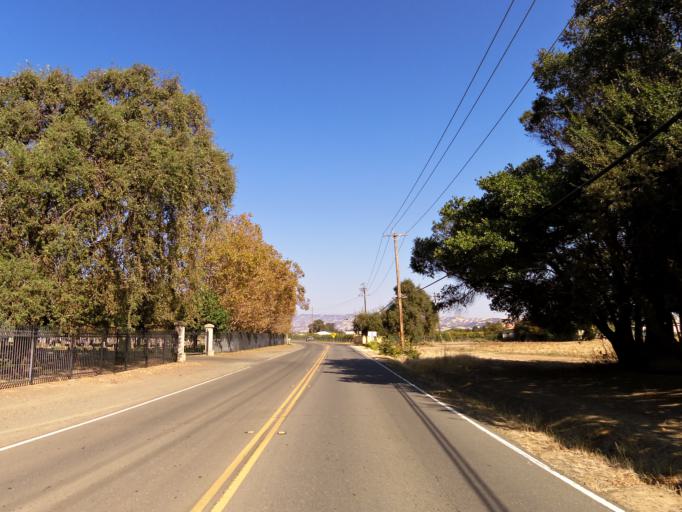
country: US
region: California
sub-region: Solano County
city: Green Valley
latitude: 38.2480
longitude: -122.1207
